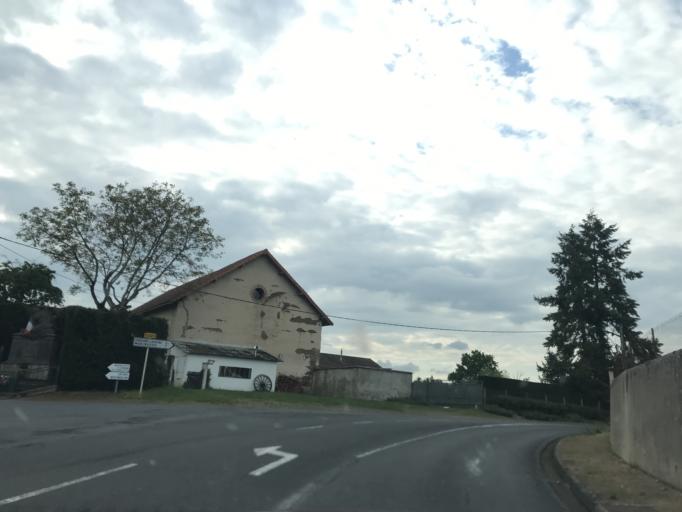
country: FR
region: Auvergne
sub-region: Departement du Puy-de-Dome
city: Orleat
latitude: 45.8942
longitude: 3.3859
